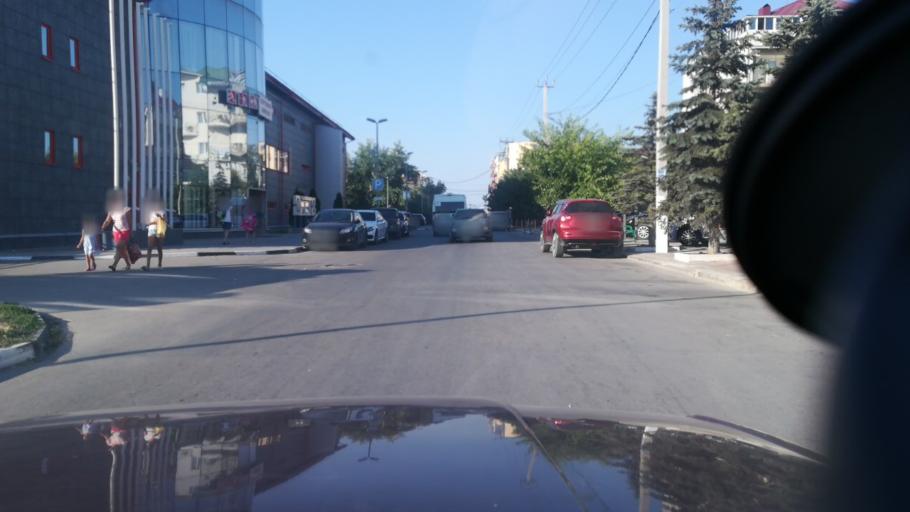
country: RU
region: Krasnodarskiy
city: Vityazevo
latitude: 44.9890
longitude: 37.2534
